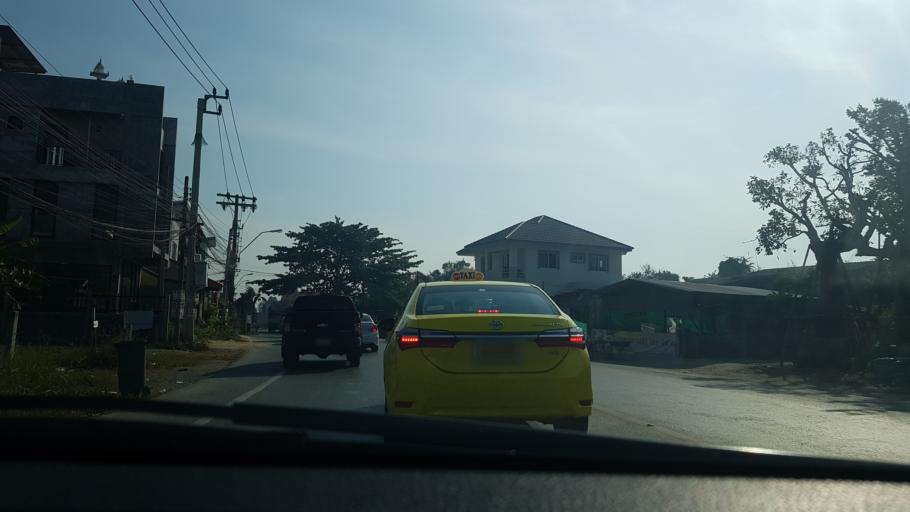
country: TH
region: Bangkok
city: Thawi Watthana
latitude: 13.7985
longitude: 100.3647
